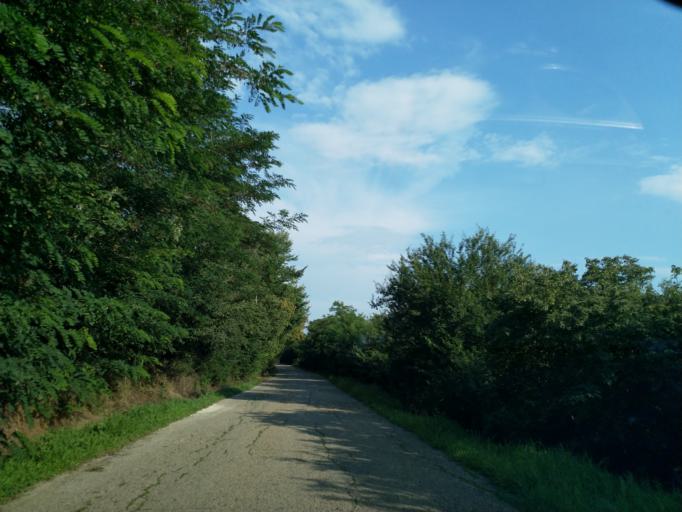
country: RS
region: Central Serbia
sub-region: Pomoravski Okrug
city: Jagodina
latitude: 43.9967
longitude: 21.1930
